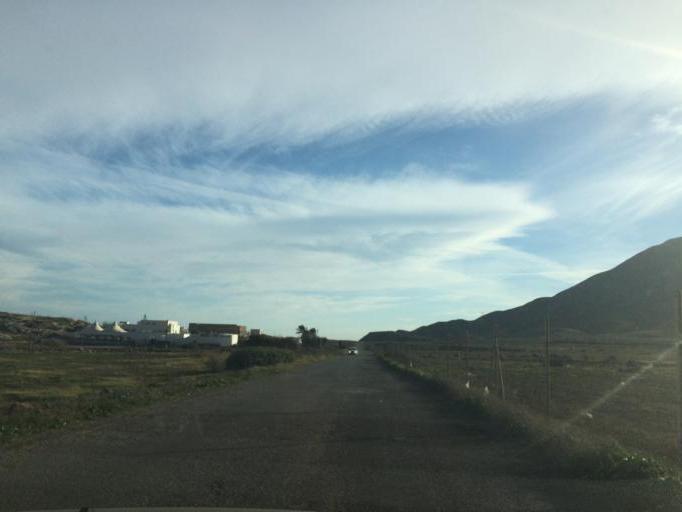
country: ES
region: Andalusia
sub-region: Provincia de Almeria
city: San Jose
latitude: 36.8060
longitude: -2.0647
